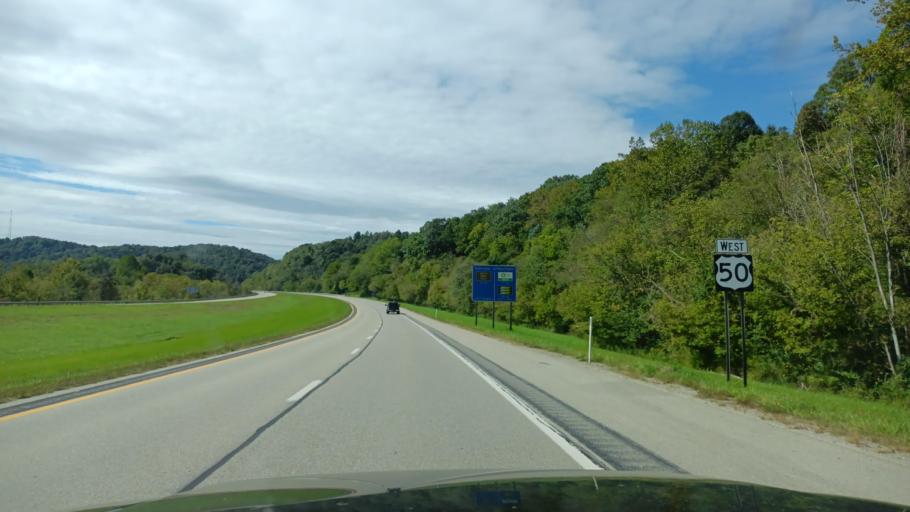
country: US
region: West Virginia
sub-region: Doddridge County
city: West Union
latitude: 39.2874
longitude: -80.7152
